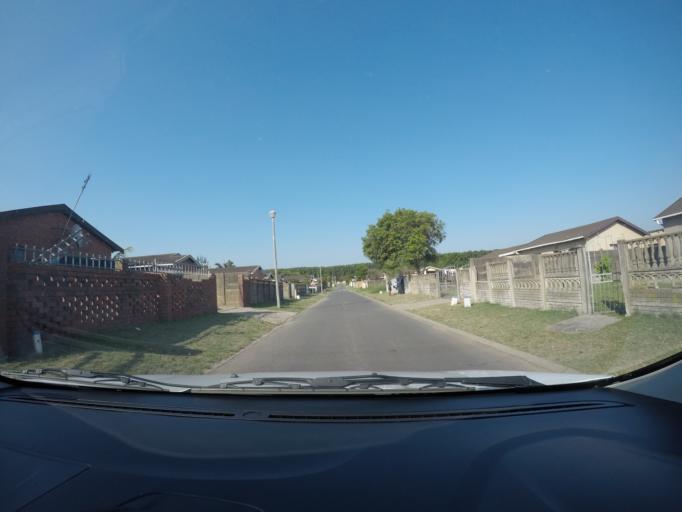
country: ZA
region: KwaZulu-Natal
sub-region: uThungulu District Municipality
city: Richards Bay
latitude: -28.7147
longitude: 32.0397
